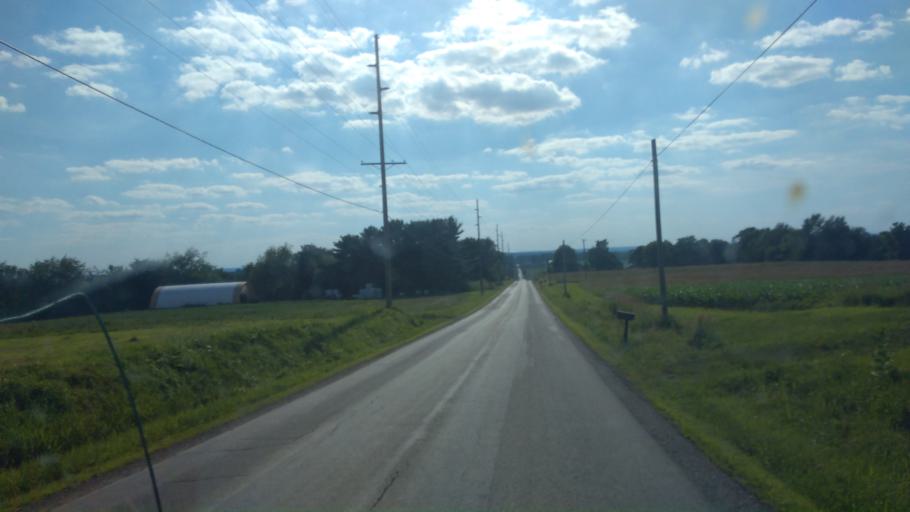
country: US
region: Ohio
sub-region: Wayne County
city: Apple Creek
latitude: 40.7112
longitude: -81.9229
